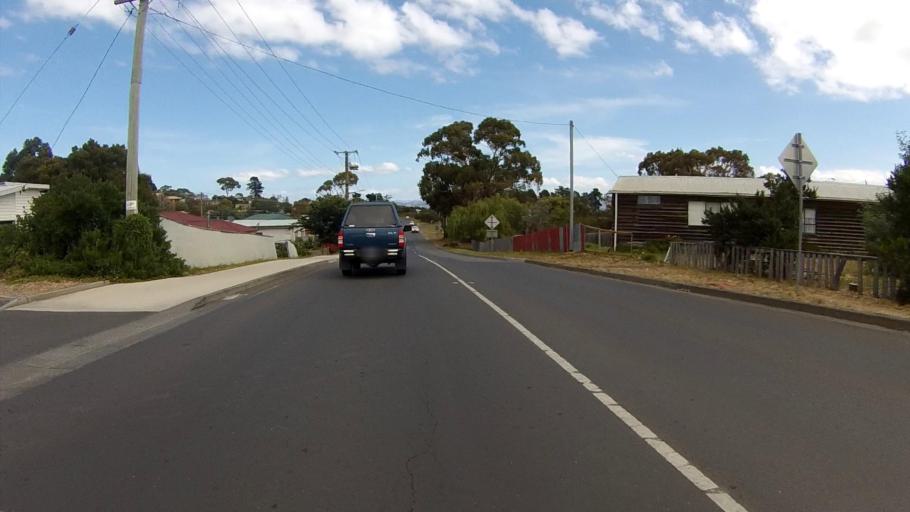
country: AU
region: Tasmania
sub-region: Sorell
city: Sorell
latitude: -42.8579
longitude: 147.6166
